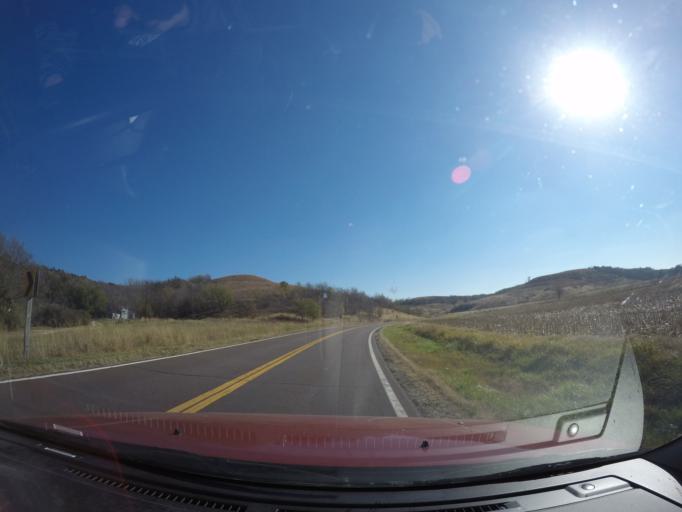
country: US
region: Kansas
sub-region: Geary County
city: Grandview Plaza
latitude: 39.0077
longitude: -96.7323
